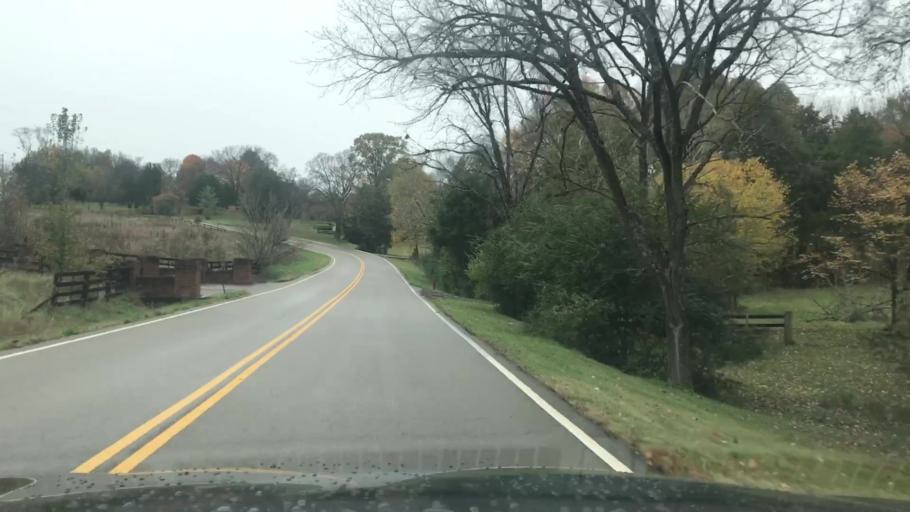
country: US
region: Tennessee
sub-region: Williamson County
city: Franklin
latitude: 35.8933
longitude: -86.8169
